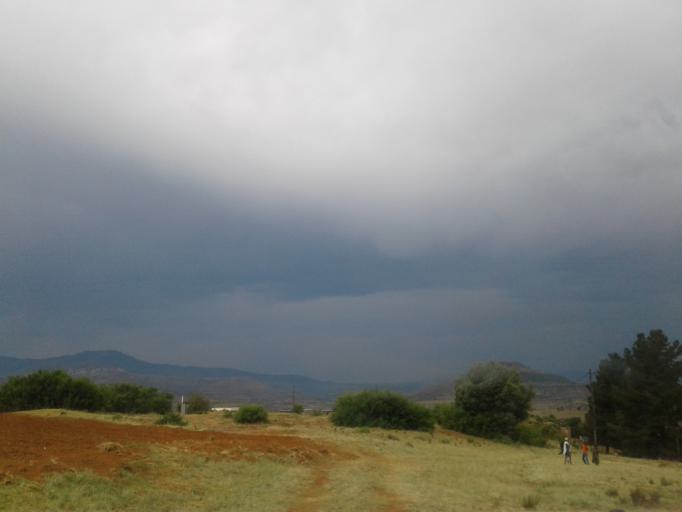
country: LS
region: Quthing
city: Quthing
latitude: -30.3789
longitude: 27.5549
